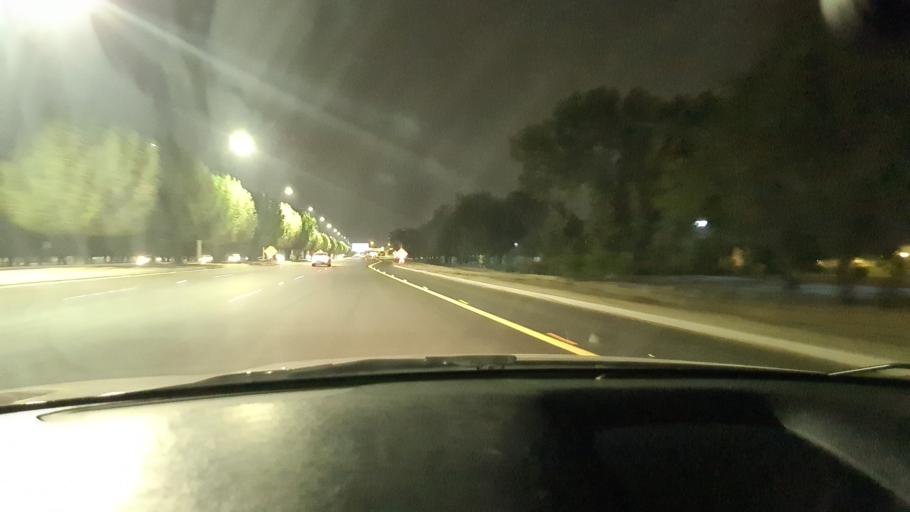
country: SA
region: Eastern Province
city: Al Jubayl
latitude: 27.1259
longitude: 49.5451
